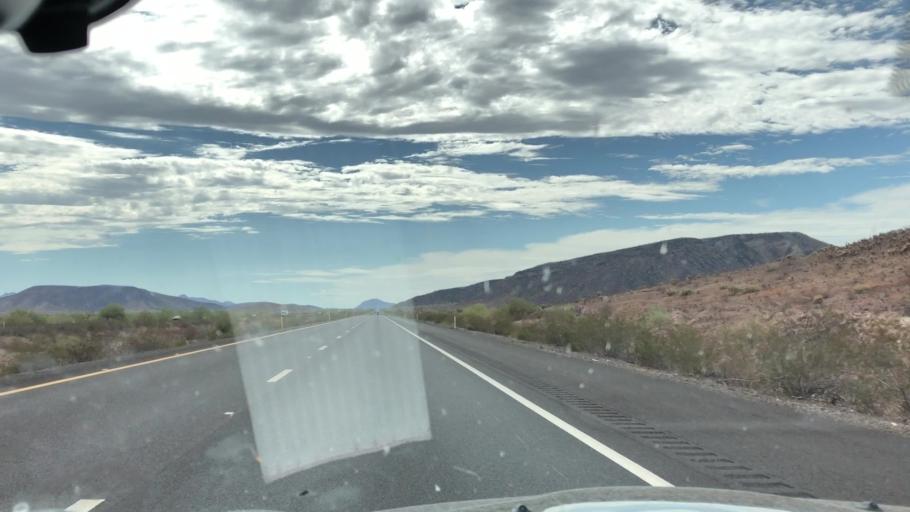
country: US
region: Arizona
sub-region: La Paz County
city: Salome
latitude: 33.6456
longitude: -113.8739
